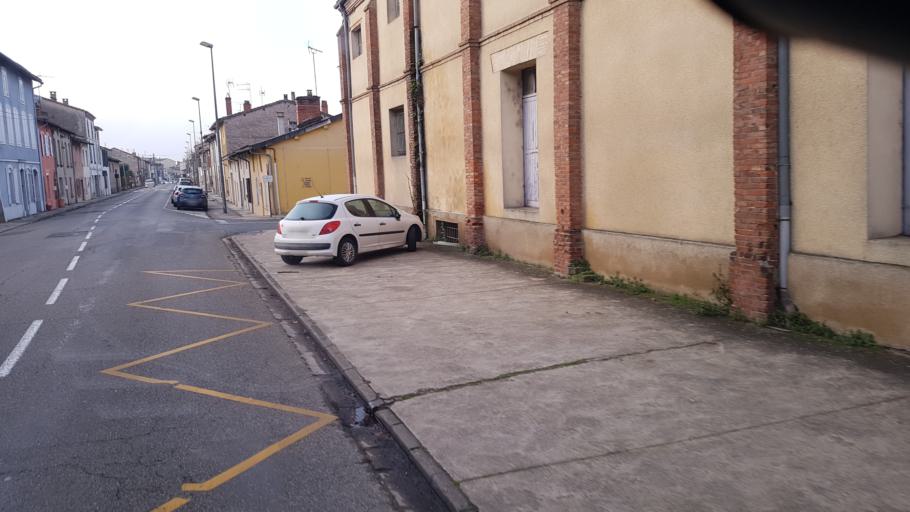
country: FR
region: Midi-Pyrenees
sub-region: Departement du Tarn
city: Gaillac
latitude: 43.9074
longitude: 1.8994
